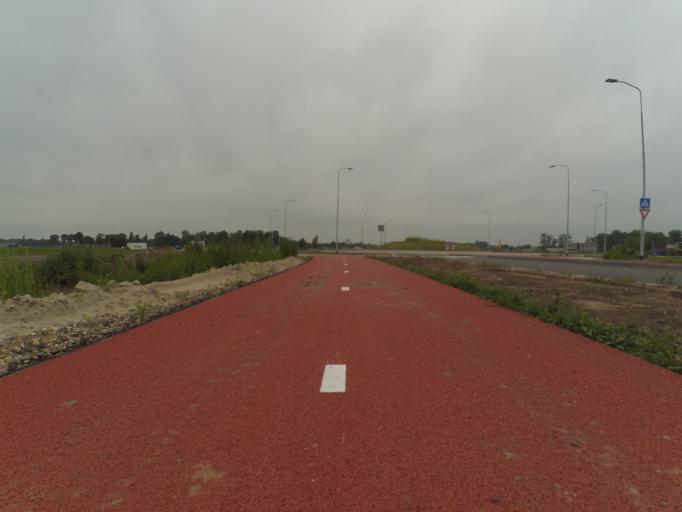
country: NL
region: Gelderland
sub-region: Gemeente Barneveld
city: Voorthuizen
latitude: 52.1608
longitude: 5.6205
